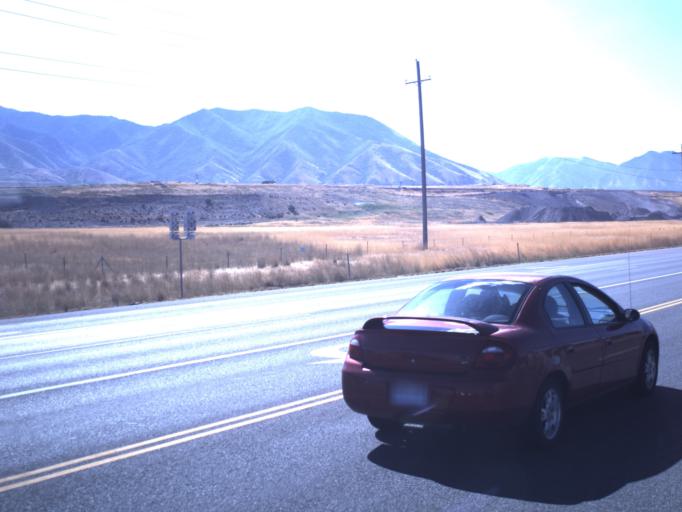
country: US
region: Utah
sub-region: Tooele County
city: Stansbury park
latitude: 40.6529
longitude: -112.2892
